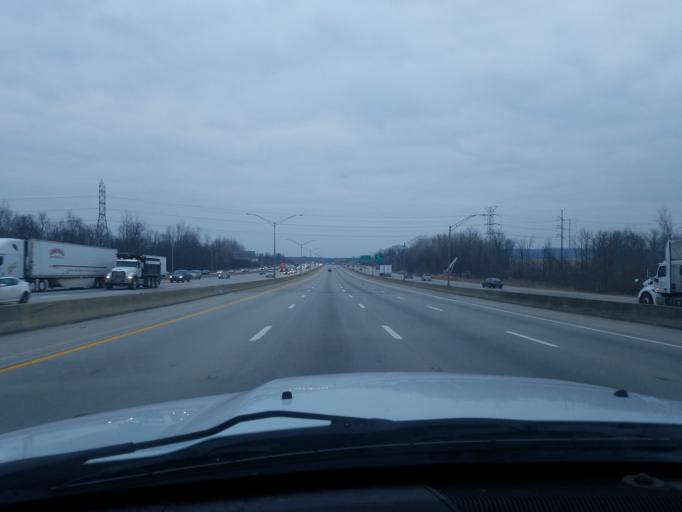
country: US
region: Kentucky
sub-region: Jefferson County
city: Heritage Creek
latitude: 38.1484
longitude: -85.7131
